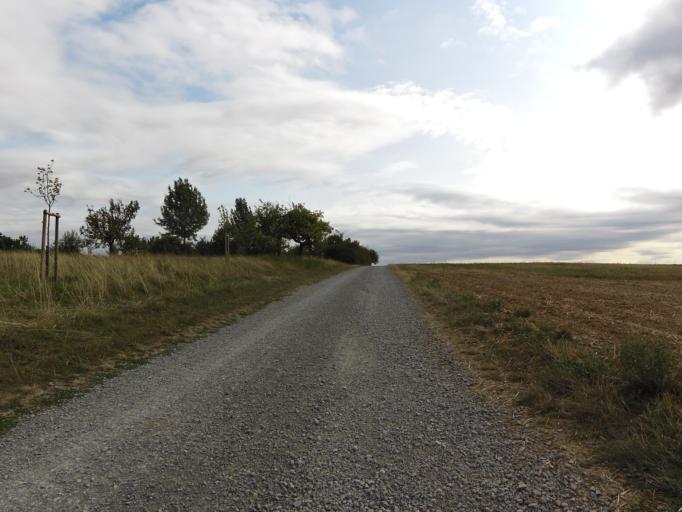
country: DE
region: Bavaria
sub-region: Regierungsbezirk Unterfranken
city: Rimpar
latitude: 49.8354
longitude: 9.9683
